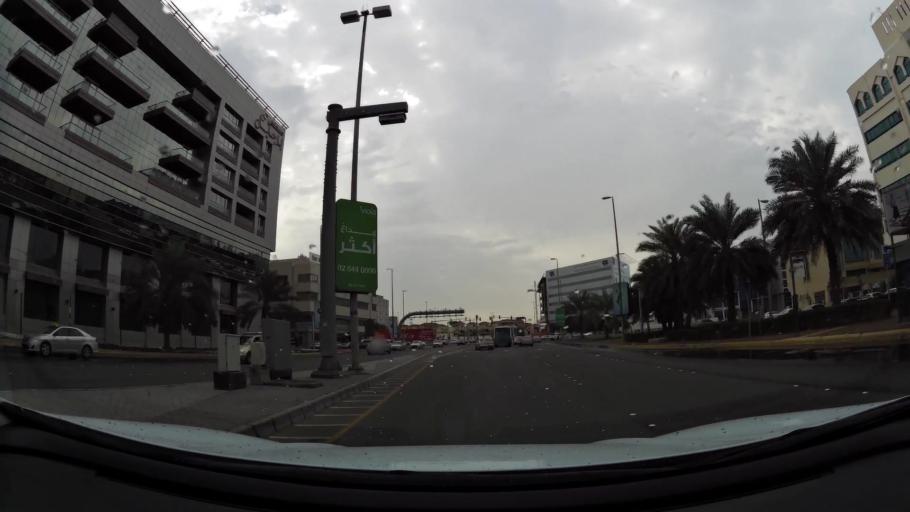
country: AE
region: Abu Dhabi
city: Abu Dhabi
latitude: 24.4788
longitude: 54.3807
